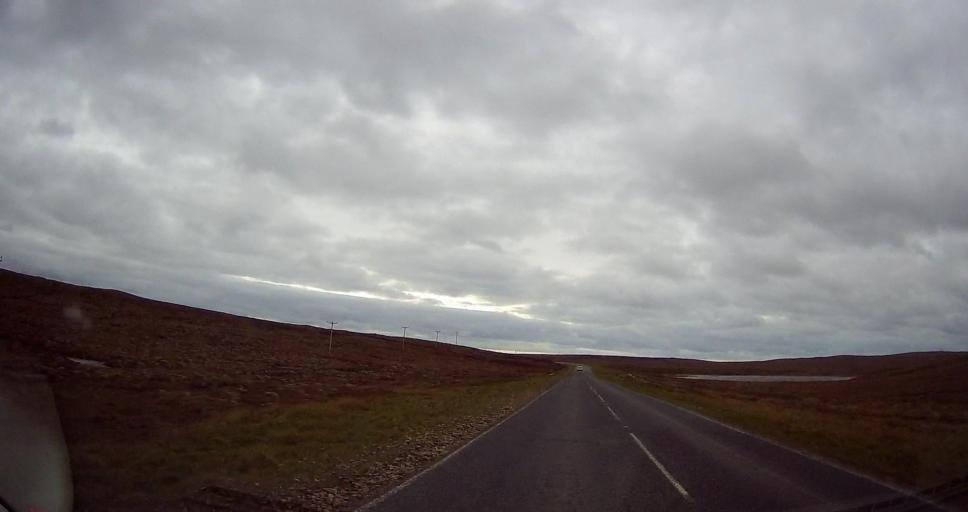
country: GB
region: Scotland
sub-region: Shetland Islands
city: Shetland
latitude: 60.6649
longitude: -1.0253
